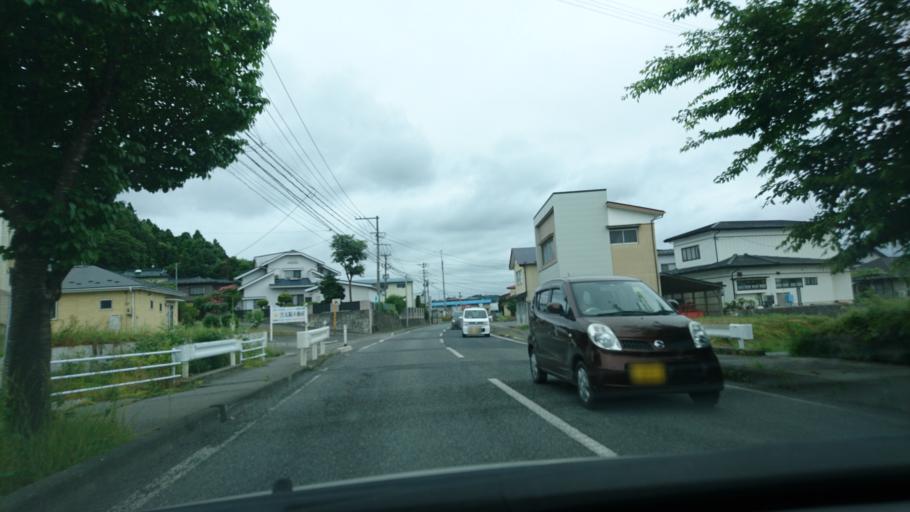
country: JP
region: Iwate
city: Ichinoseki
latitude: 38.9296
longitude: 141.1567
